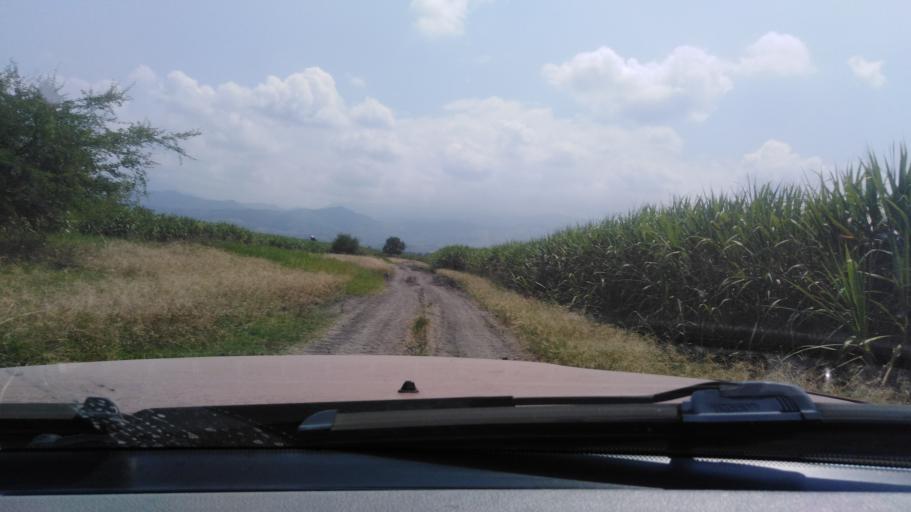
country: CO
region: Valle del Cauca
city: San Pedro
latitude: 3.9983
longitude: -76.2743
